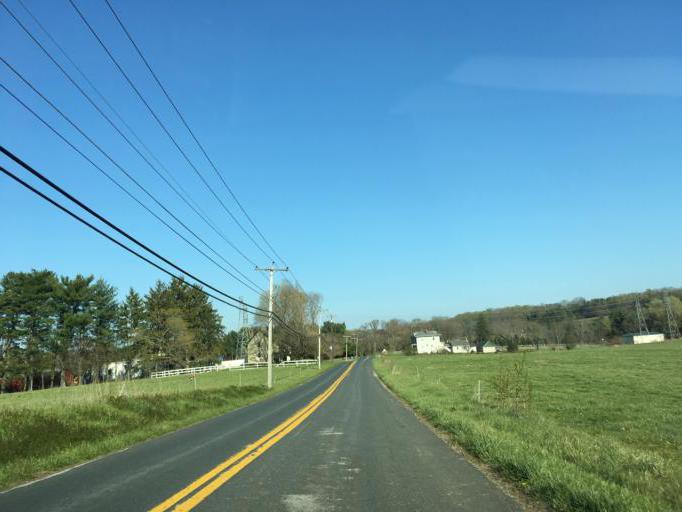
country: US
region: Maryland
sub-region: Baltimore County
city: Perry Hall
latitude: 39.4711
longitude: -76.5071
